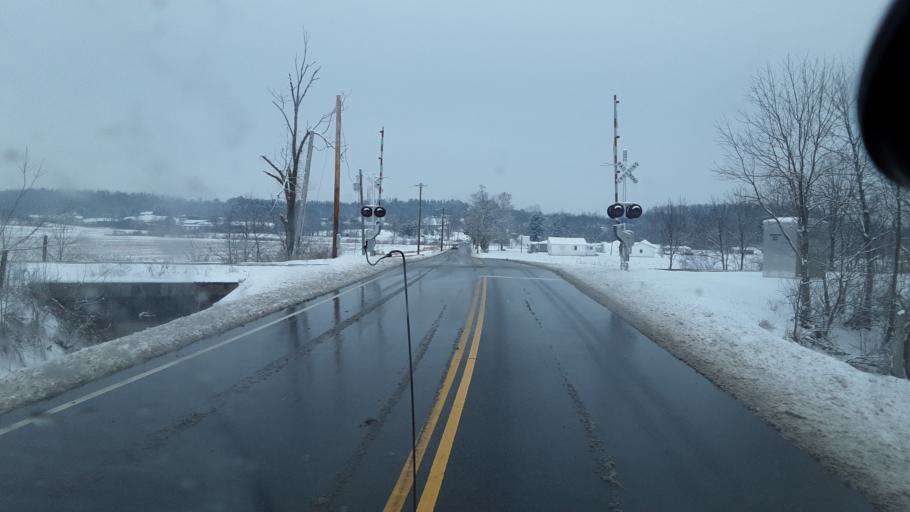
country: US
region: Ohio
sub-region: Licking County
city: Heath
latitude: 40.0316
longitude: -82.4797
